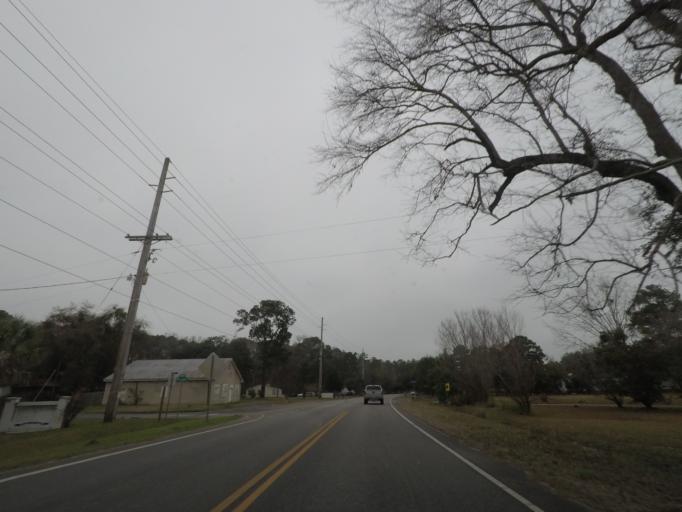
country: US
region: South Carolina
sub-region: Charleston County
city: Meggett
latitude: 32.5844
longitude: -80.3460
